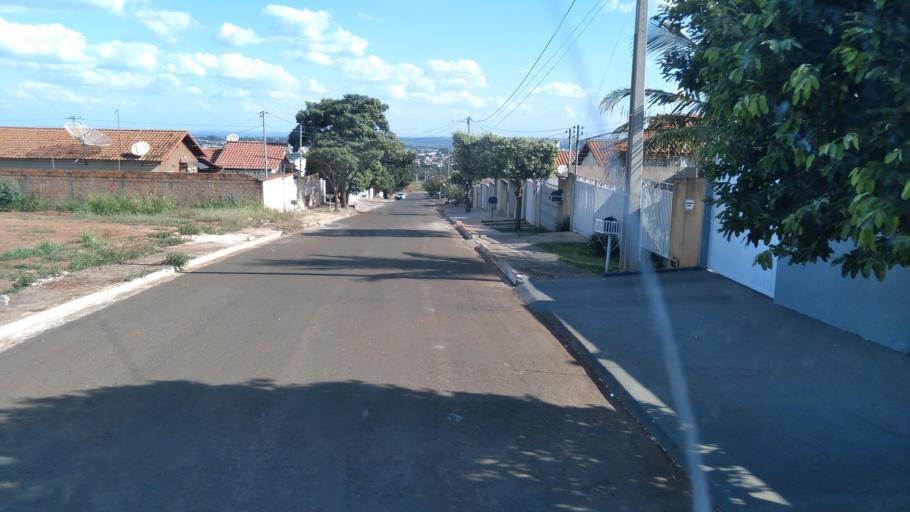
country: YE
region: Al Mahrah
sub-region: Shahan
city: Shihan as Sufla
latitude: 17.5492
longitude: 52.5385
